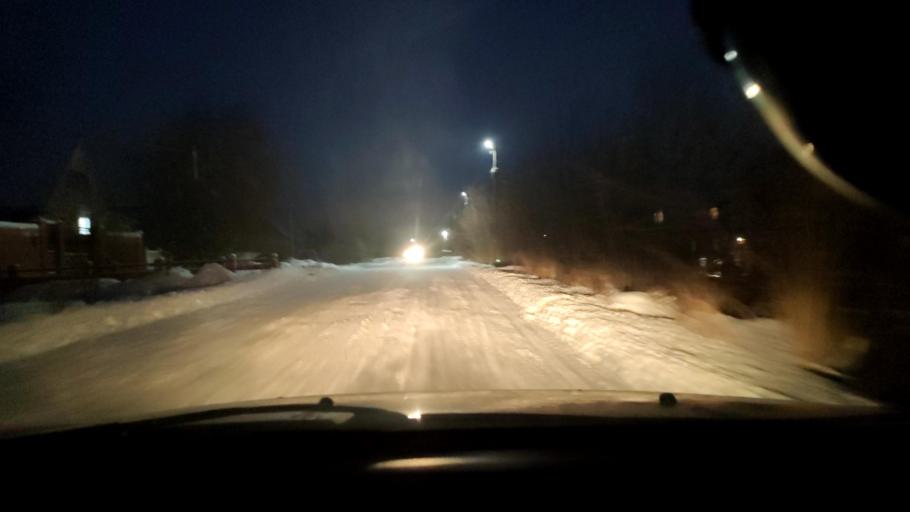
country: RU
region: Perm
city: Kultayevo
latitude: 57.9250
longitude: 55.8749
